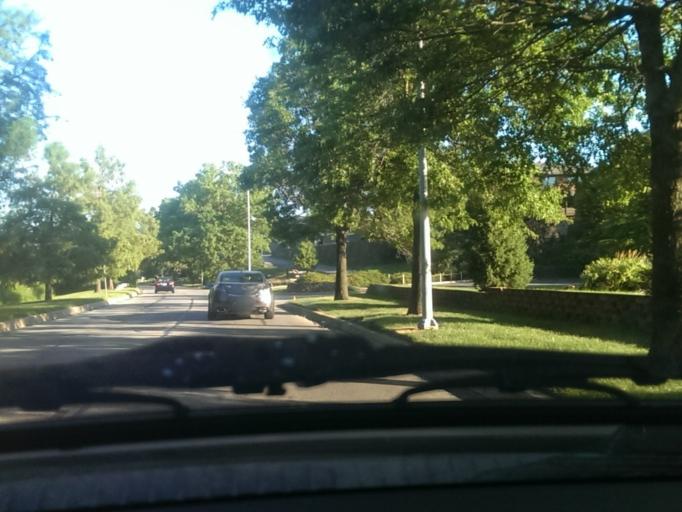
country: US
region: Kansas
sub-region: Johnson County
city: Leawood
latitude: 38.9648
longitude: -94.6051
